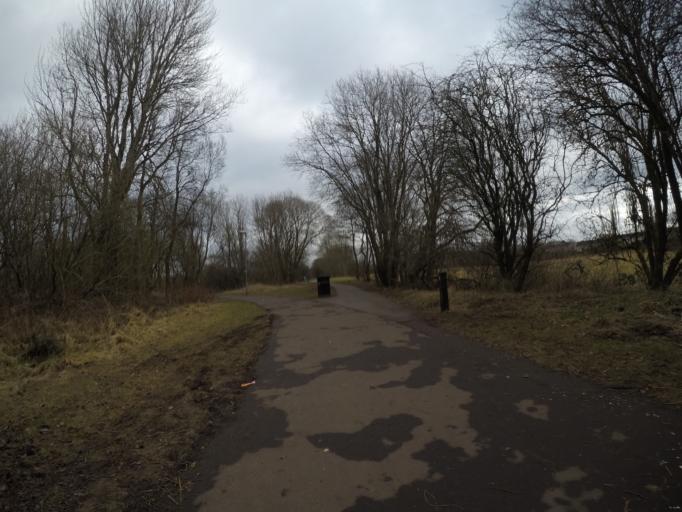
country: GB
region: Scotland
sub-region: North Ayrshire
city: Dreghorn
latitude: 55.6102
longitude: -4.6277
